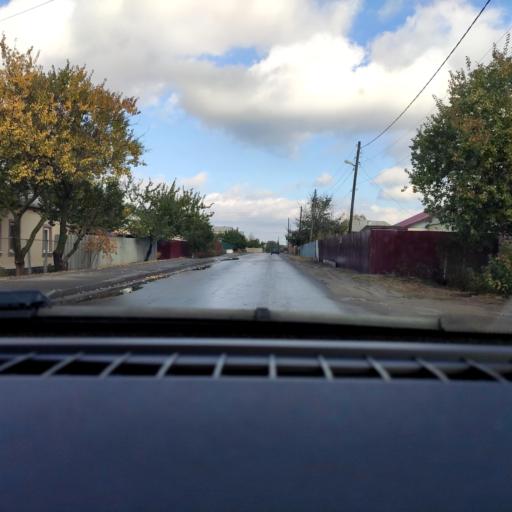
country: RU
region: Voronezj
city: Maslovka
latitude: 51.6087
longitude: 39.2207
